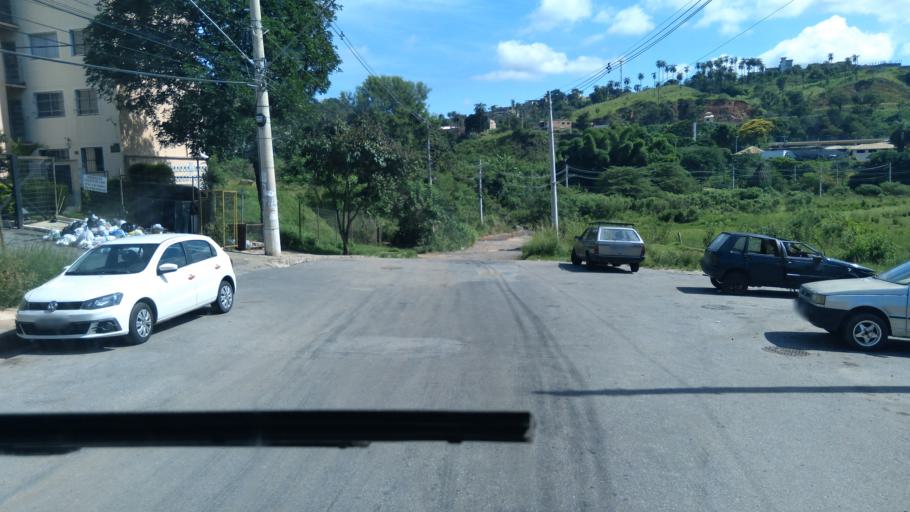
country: BR
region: Minas Gerais
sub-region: Santa Luzia
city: Santa Luzia
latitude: -19.8423
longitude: -43.8780
